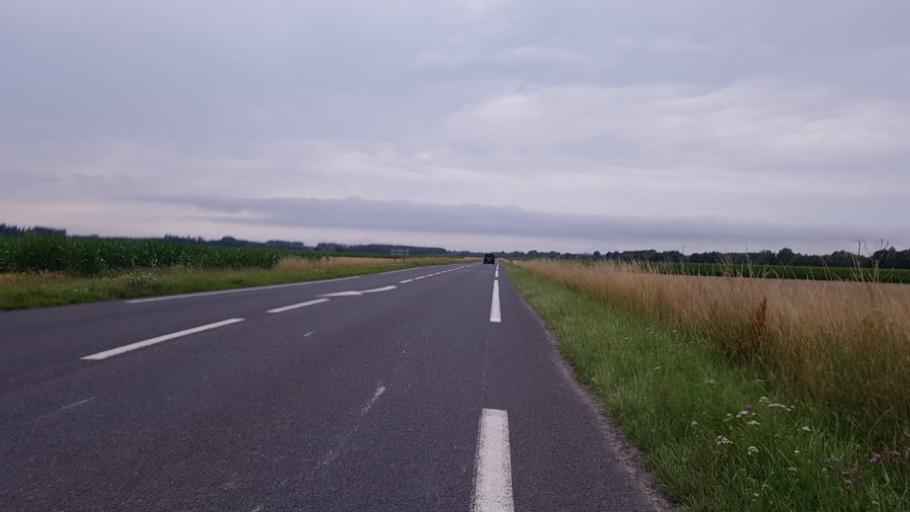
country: FR
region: Champagne-Ardenne
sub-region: Departement de la Marne
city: Pargny-sur-Saulx
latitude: 48.7578
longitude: 4.7461
